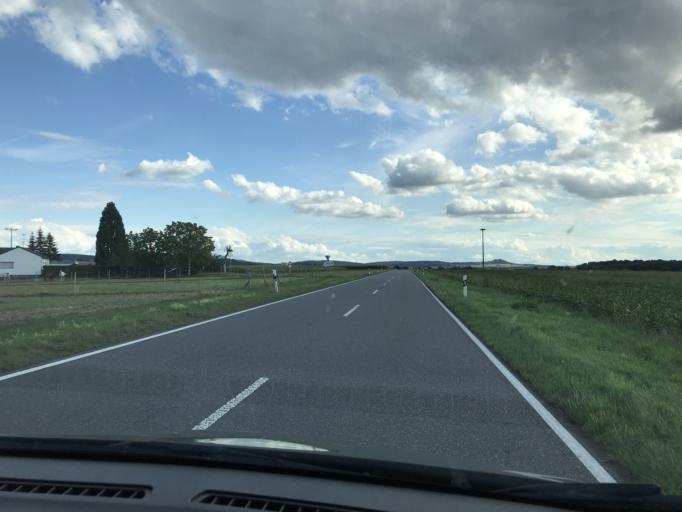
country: DE
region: Hesse
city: Gross-Umstadt
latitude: 49.9036
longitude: 8.9177
